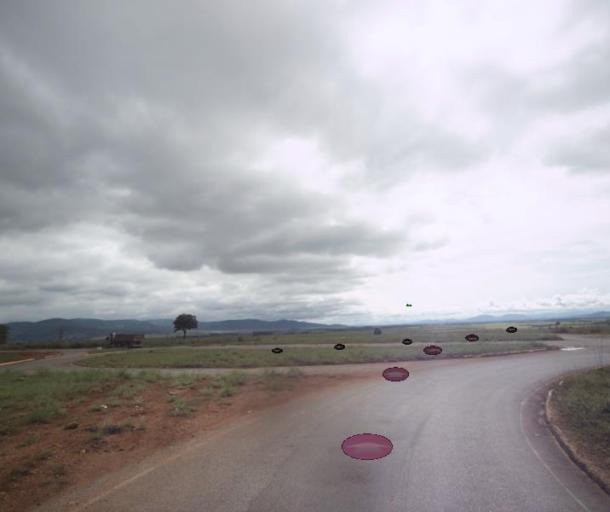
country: BR
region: Goias
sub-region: Barro Alto
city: Barro Alto
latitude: -15.0239
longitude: -48.8968
